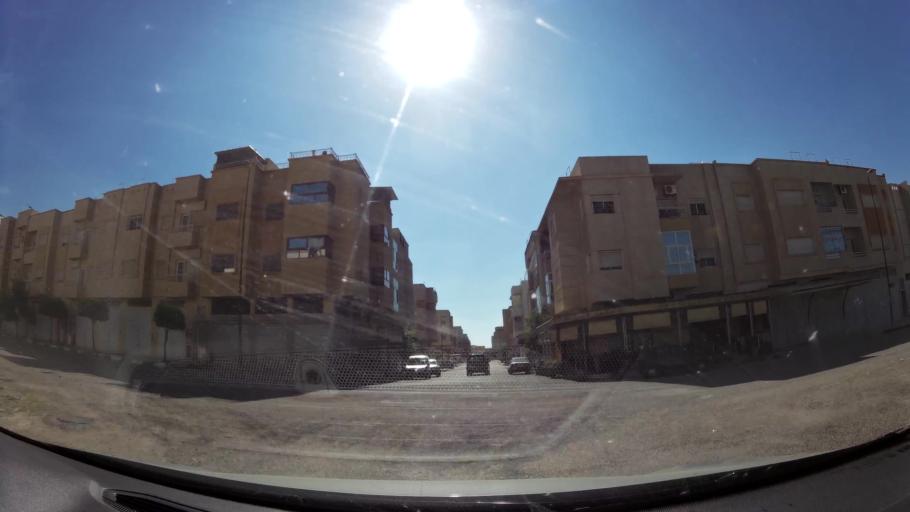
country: MA
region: Fes-Boulemane
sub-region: Fes
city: Fes
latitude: 34.0000
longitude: -5.0045
